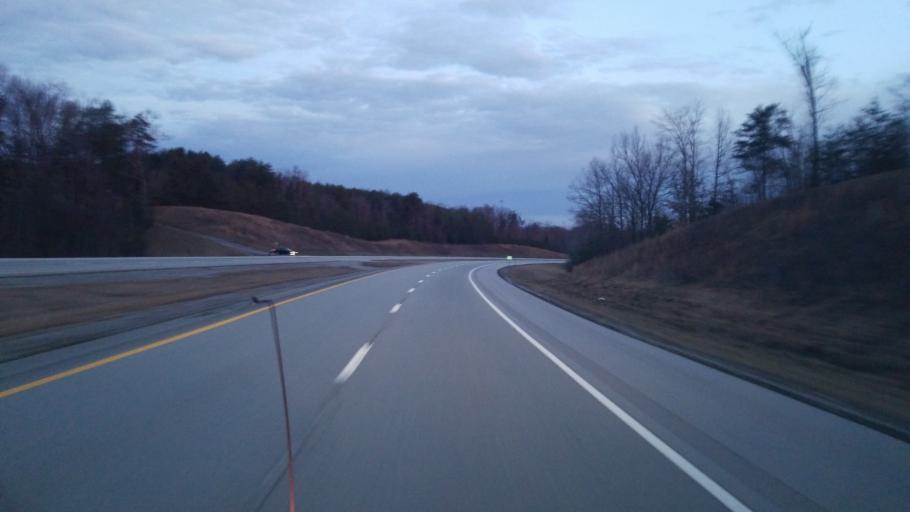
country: US
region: Tennessee
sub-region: Van Buren County
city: Spencer
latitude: 35.6922
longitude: -85.4807
